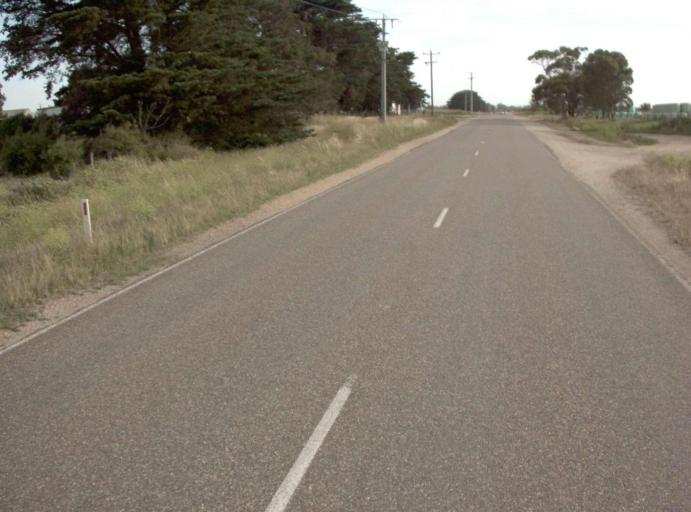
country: AU
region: Victoria
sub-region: Wellington
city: Heyfield
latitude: -37.9831
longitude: 146.8877
